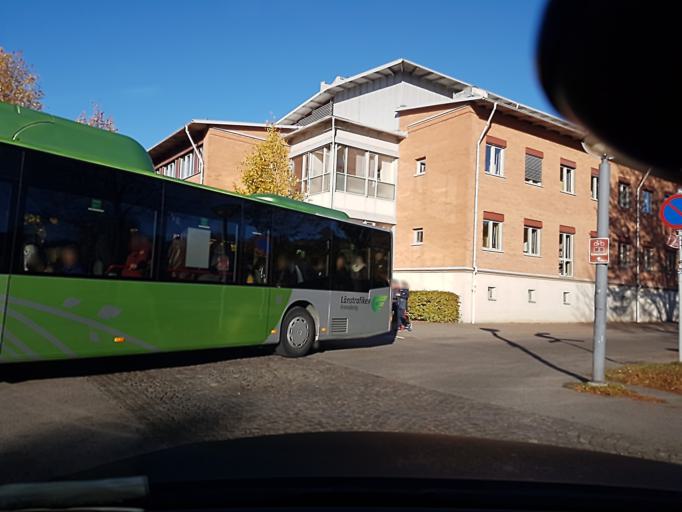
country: SE
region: Kronoberg
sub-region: Vaxjo Kommun
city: Vaexjoe
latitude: 56.8551
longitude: 14.8314
